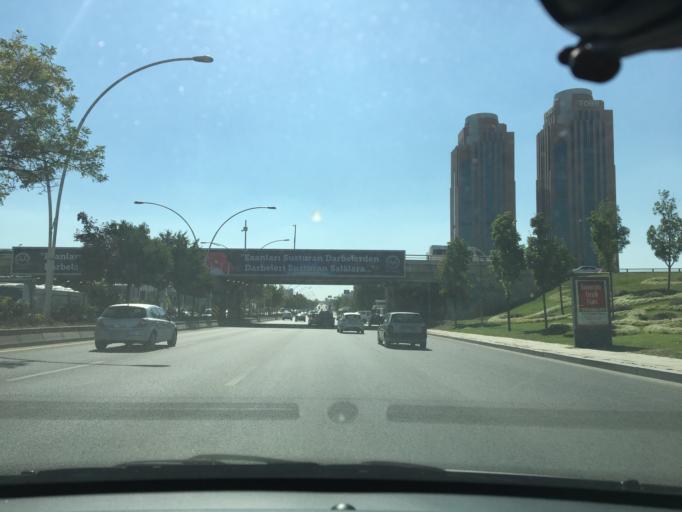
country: TR
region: Ankara
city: Batikent
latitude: 39.9079
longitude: 32.7651
